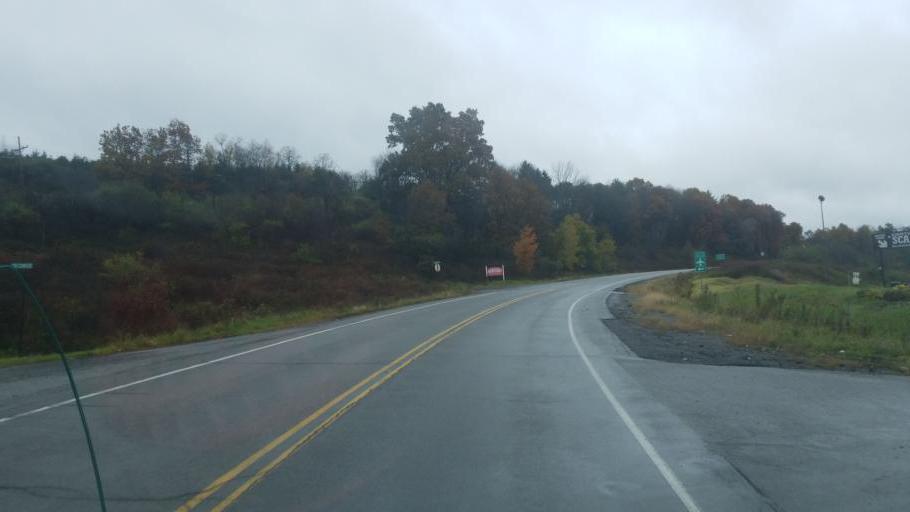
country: US
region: Pennsylvania
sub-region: Clearfield County
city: Clearfield
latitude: 41.0437
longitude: -78.3947
